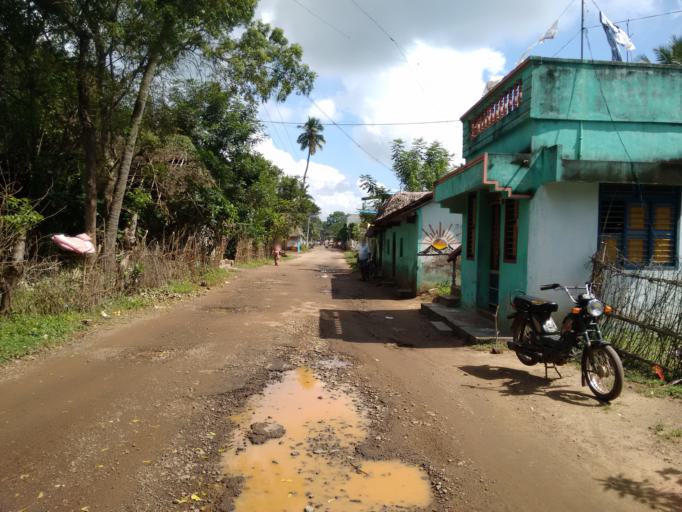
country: IN
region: Tamil Nadu
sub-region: Thiruvarur
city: Koradachcheri
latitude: 10.8482
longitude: 79.5092
